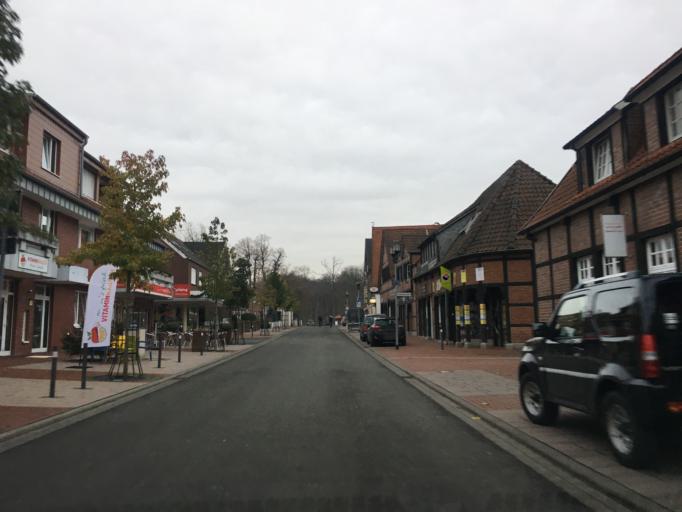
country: DE
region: North Rhine-Westphalia
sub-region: Regierungsbezirk Munster
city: Nordkirchen
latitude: 51.7378
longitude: 7.5268
